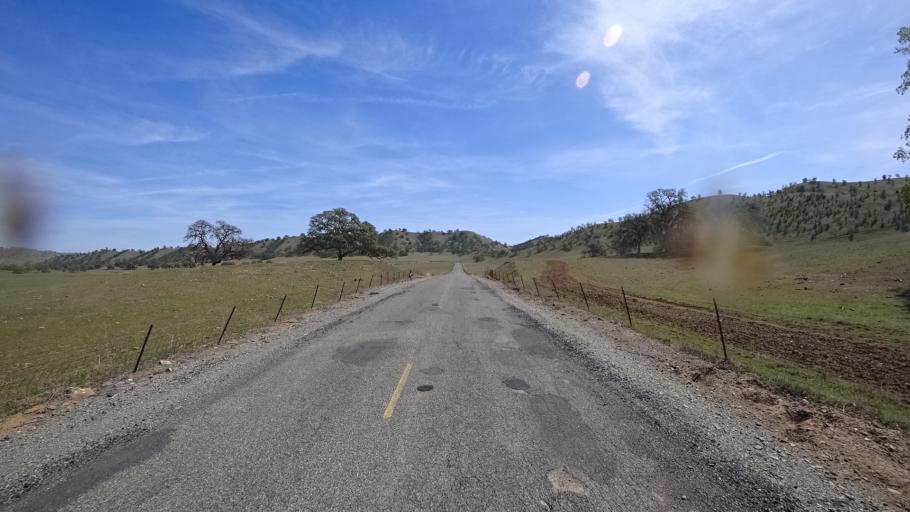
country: US
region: California
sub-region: Glenn County
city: Willows
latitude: 39.5383
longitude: -122.4482
